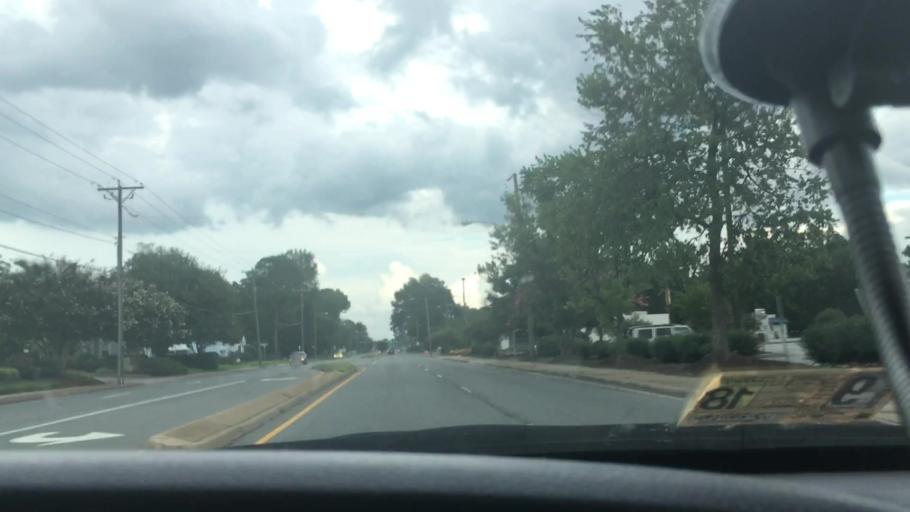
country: US
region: Virginia
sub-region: City of Portsmouth
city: Portsmouth Heights
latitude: 36.8193
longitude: -76.3789
